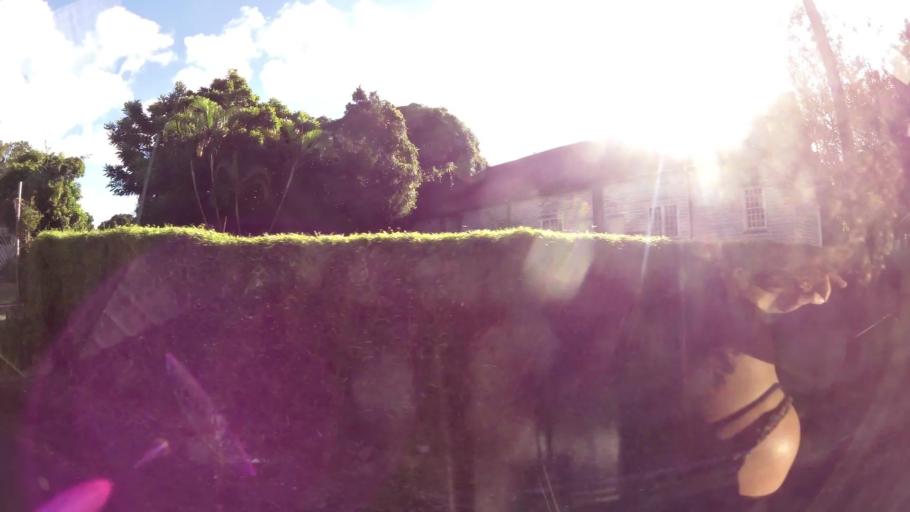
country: MU
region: Plaines Wilhems
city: Vacoas
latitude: -20.2904
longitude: 57.4965
